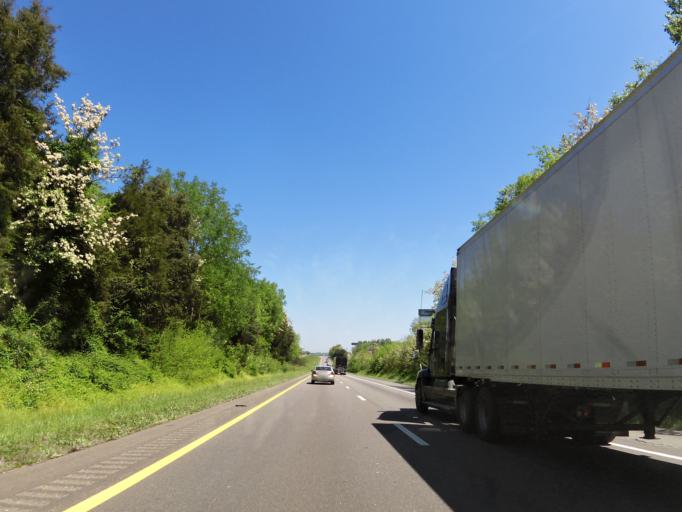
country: US
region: Tennessee
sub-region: Jefferson County
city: White Pine
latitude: 36.0991
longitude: -83.3457
